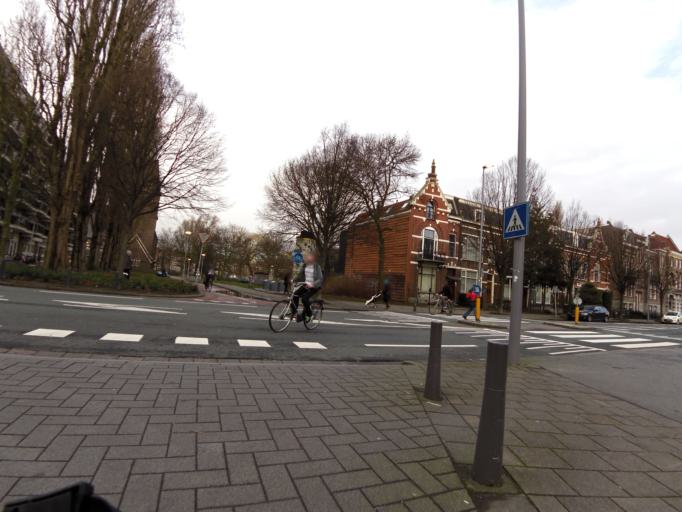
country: NL
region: South Holland
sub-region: Gemeente Rotterdam
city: Rotterdam
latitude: 51.9286
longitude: 4.4667
